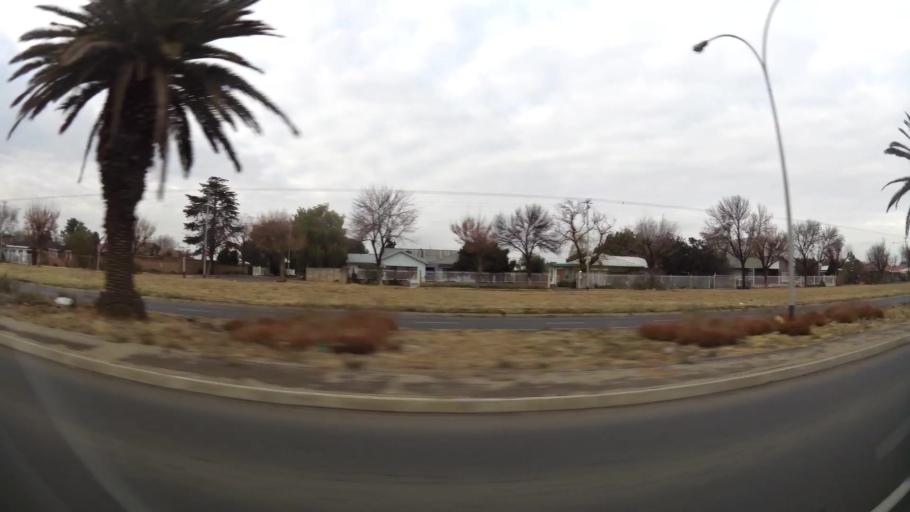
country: ZA
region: Orange Free State
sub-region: Mangaung Metropolitan Municipality
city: Bloemfontein
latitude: -29.1265
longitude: 26.1723
